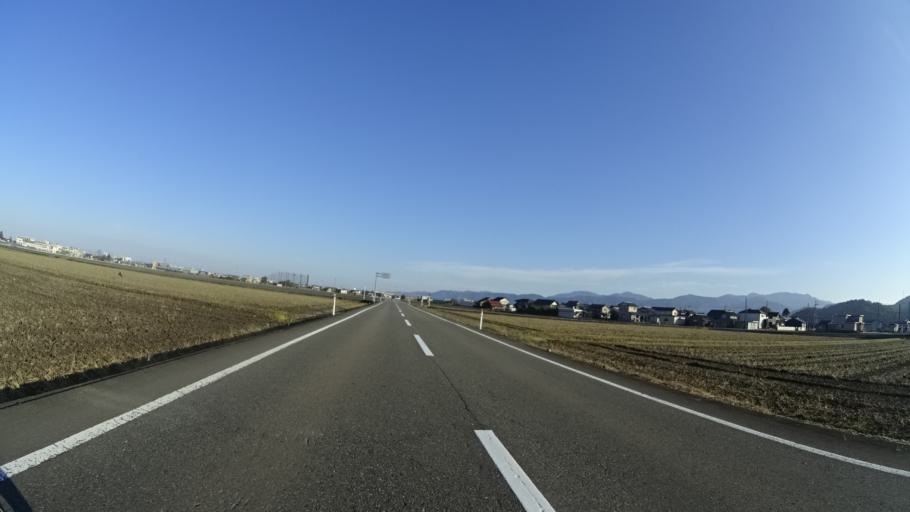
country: JP
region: Fukui
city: Fukui-shi
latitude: 36.0739
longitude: 136.2575
